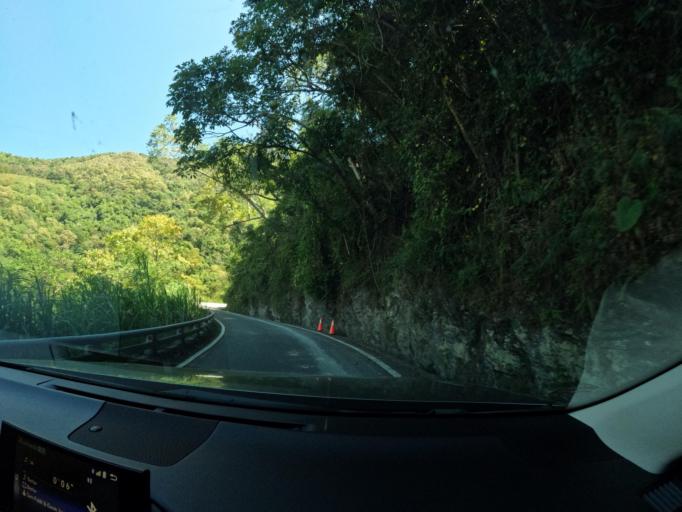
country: TW
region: Taiwan
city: Yujing
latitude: 23.2730
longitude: 120.8456
